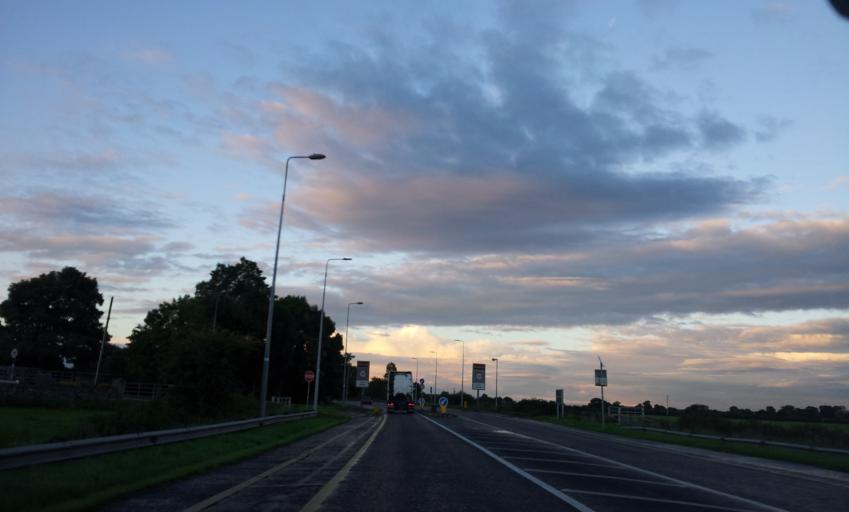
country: IE
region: Munster
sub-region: County Limerick
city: Rathkeale
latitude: 52.5354
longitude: -8.8667
